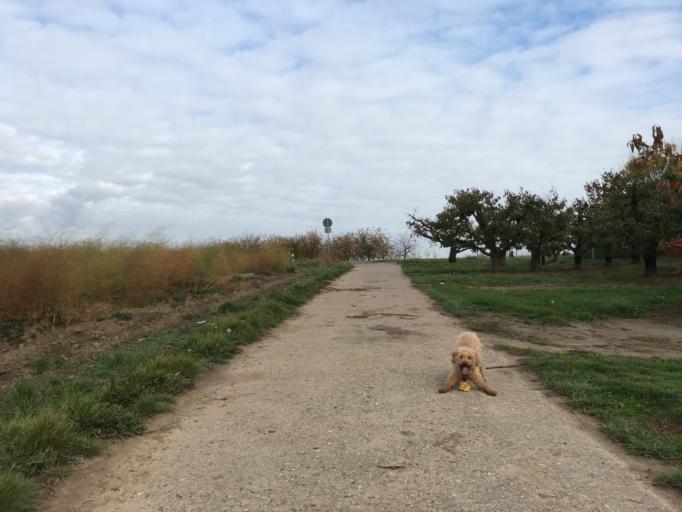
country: DE
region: Rheinland-Pfalz
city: Budenheim
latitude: 49.9808
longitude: 8.1592
